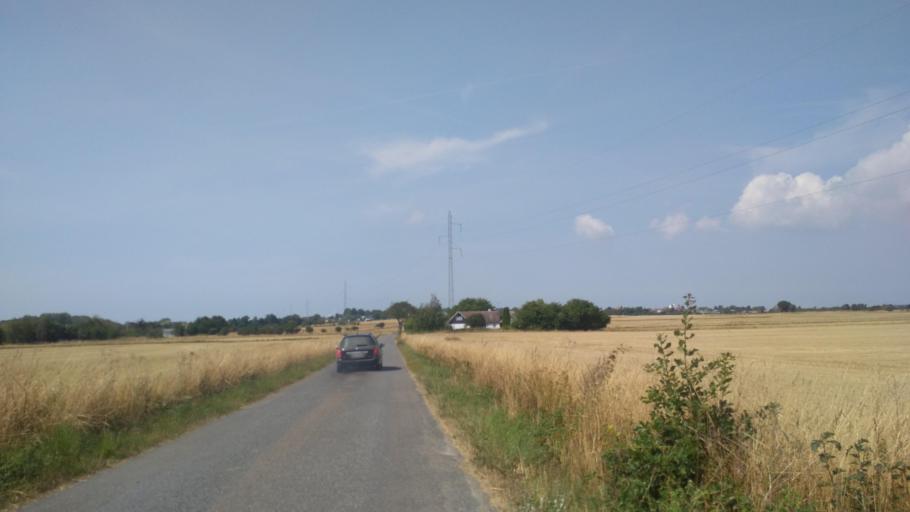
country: DK
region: Capital Region
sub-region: Bornholm Kommune
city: Akirkeby
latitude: 55.0624
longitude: 14.9429
